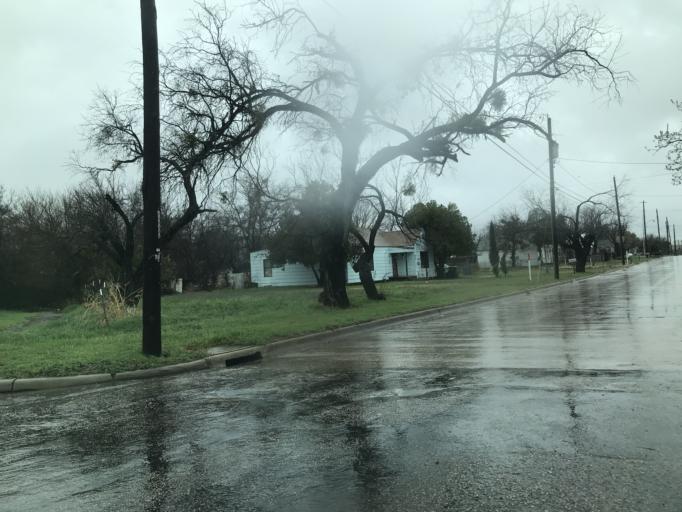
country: US
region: Texas
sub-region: Tom Green County
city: San Angelo
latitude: 31.4652
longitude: -100.4228
